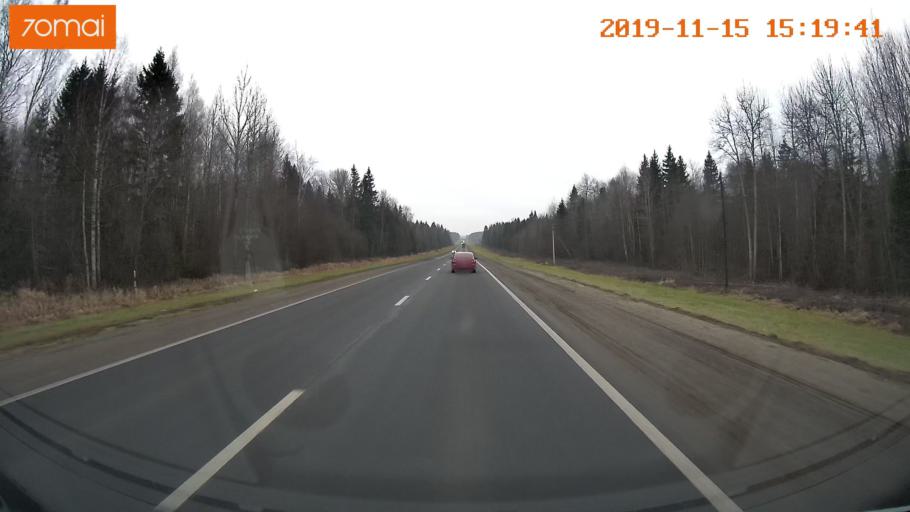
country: RU
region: Jaroslavl
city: Danilov
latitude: 58.2316
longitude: 40.1736
